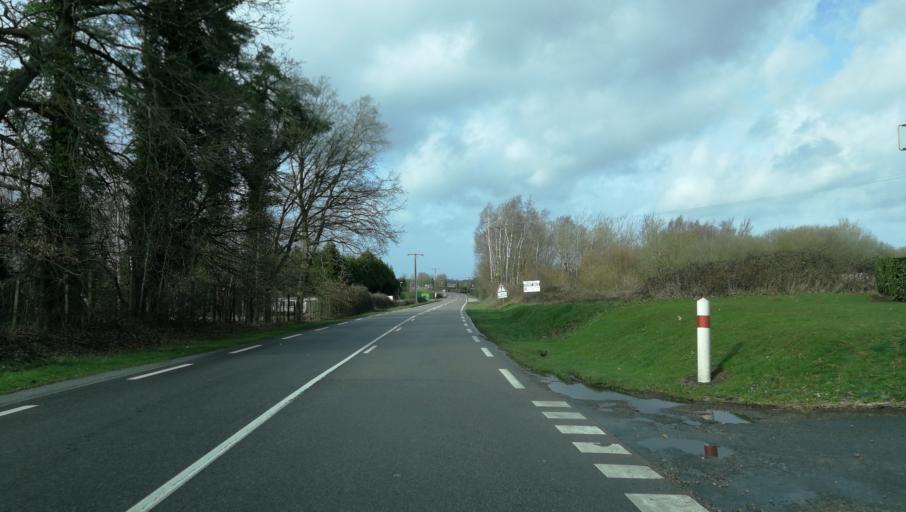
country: FR
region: Haute-Normandie
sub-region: Departement de l'Eure
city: Beuzeville
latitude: 49.3220
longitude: 0.3746
